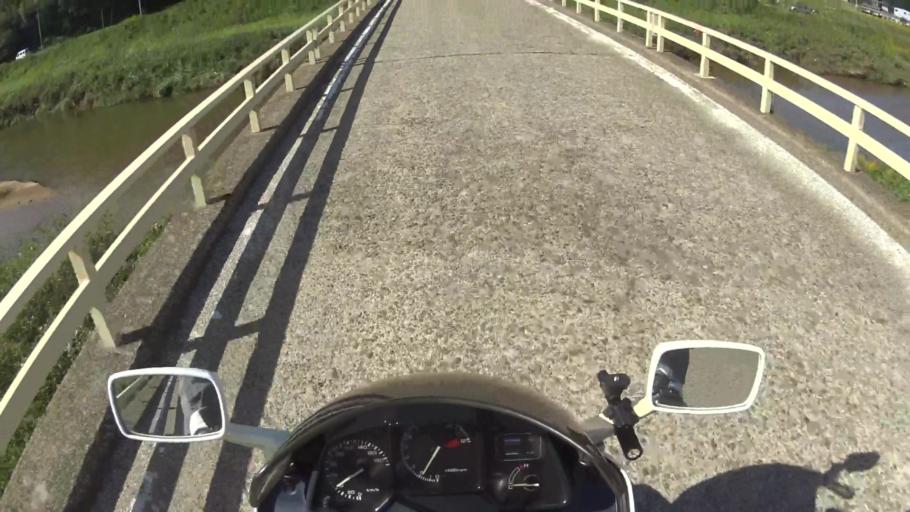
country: JP
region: Kyoto
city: Miyazu
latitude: 35.7074
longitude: 135.1034
